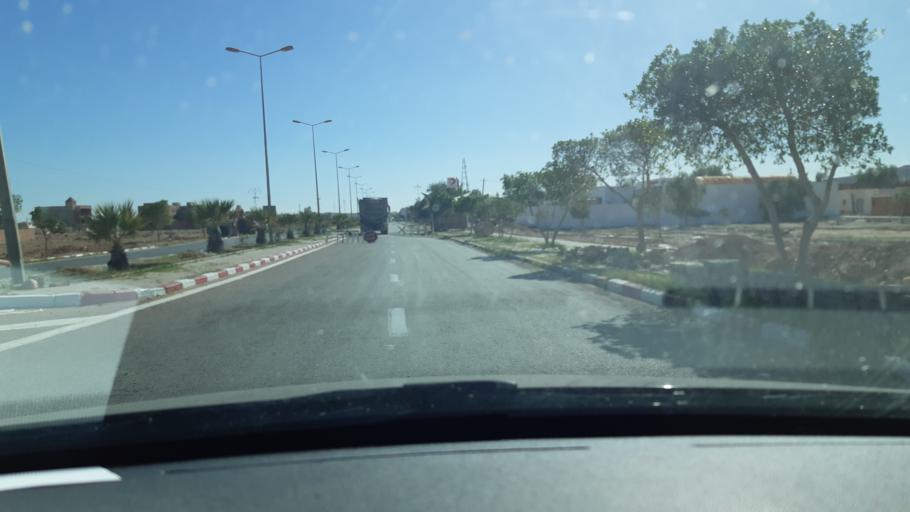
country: TN
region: Tataouine
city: Tataouine
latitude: 33.0020
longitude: 10.4644
